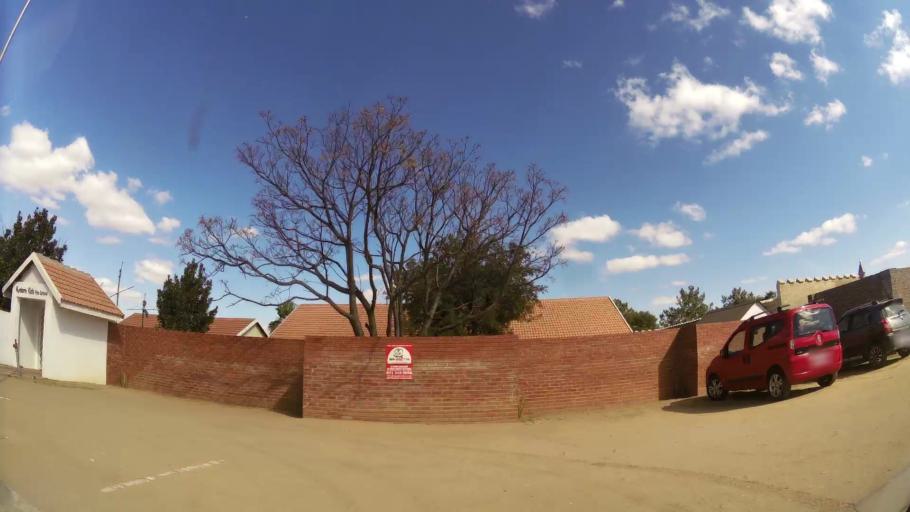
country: ZA
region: Gauteng
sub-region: City of Johannesburg Metropolitan Municipality
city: Midrand
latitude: -26.0011
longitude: 28.0942
